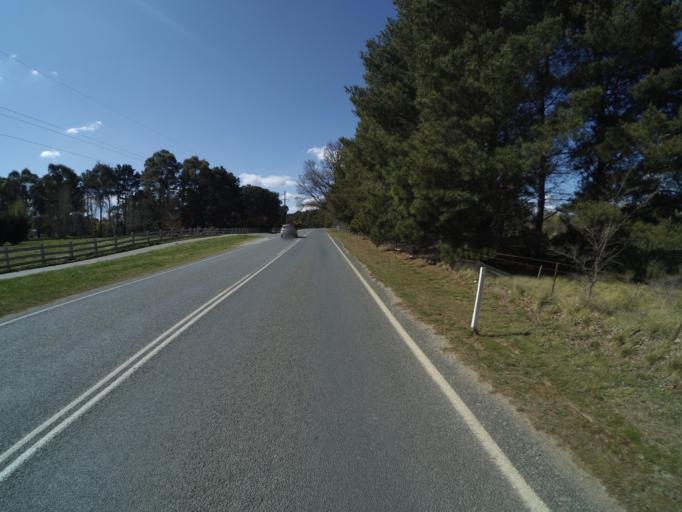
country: AU
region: New South Wales
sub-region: Palerang
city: Bungendore
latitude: -35.2495
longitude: 149.4397
